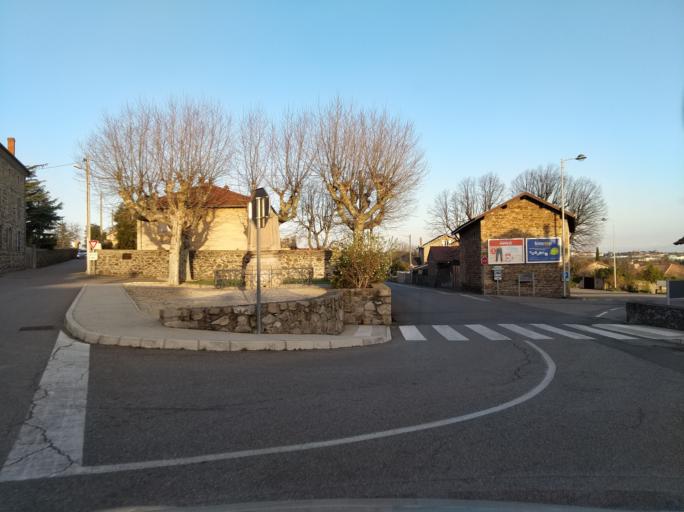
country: FR
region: Rhone-Alpes
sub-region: Departement de l'Ardeche
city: Boulieu-les-Annonay
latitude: 45.2714
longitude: 4.6687
